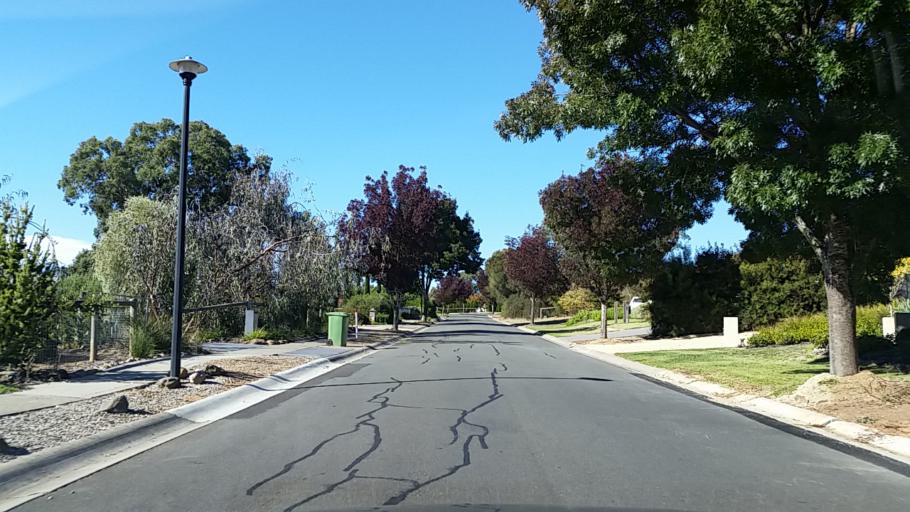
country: AU
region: South Australia
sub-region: Mount Barker
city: Mount Barker
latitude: -35.0587
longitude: 138.8781
